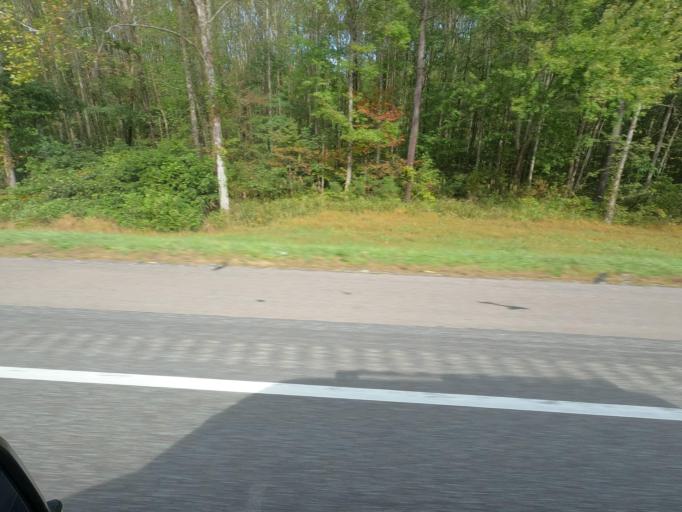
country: US
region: Tennessee
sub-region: Decatur County
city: Parsons
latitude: 35.8179
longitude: -88.2408
